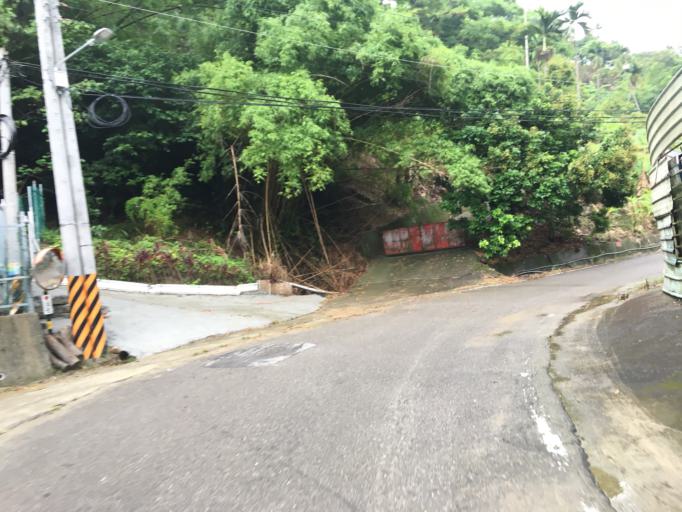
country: TW
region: Taiwan
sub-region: Taichung City
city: Taichung
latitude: 24.0600
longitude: 120.7458
